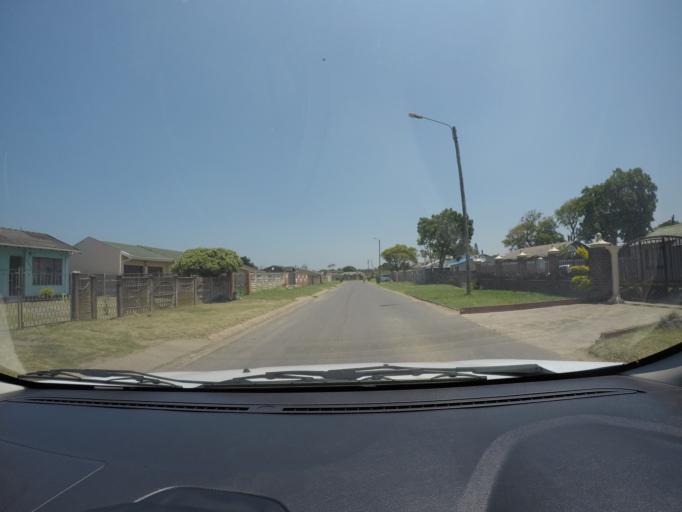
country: ZA
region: KwaZulu-Natal
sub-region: uThungulu District Municipality
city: eSikhawini
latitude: -28.8870
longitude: 31.8894
